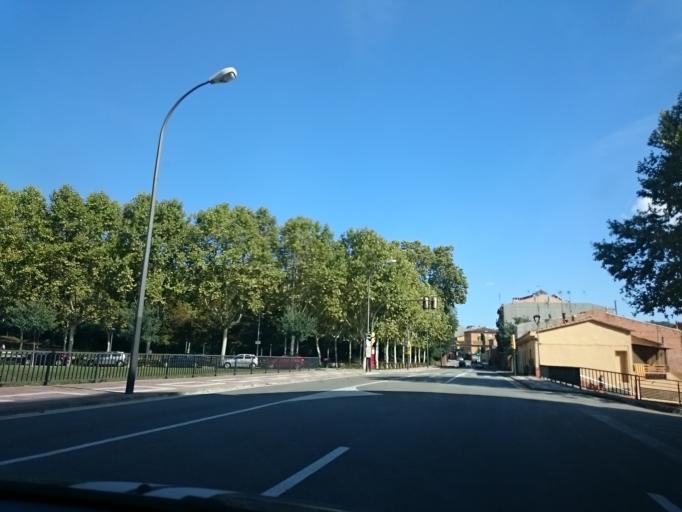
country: ES
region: Catalonia
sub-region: Provincia de Barcelona
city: Llinars del Valles
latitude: 41.6398
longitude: 2.4016
